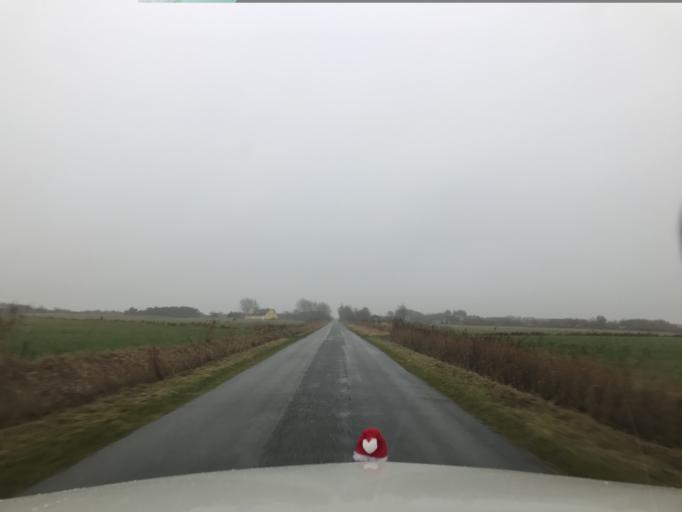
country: DK
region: South Denmark
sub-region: Esbjerg Kommune
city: Tjaereborg
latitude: 55.2836
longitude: 8.5541
